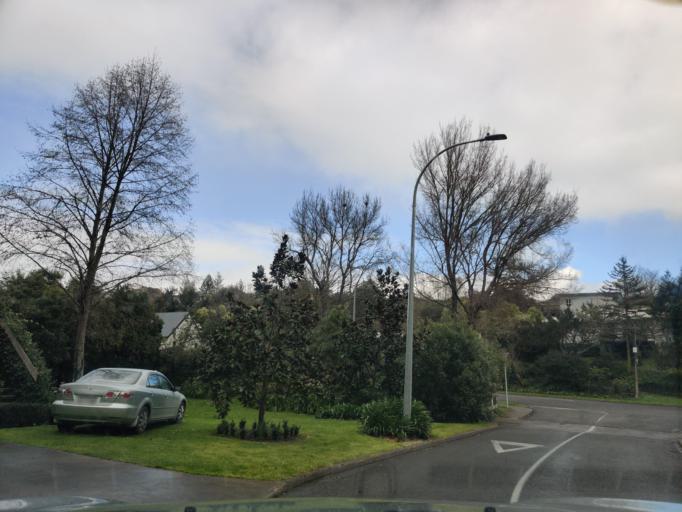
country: NZ
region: Hawke's Bay
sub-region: Hastings District
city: Hastings
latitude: -39.6760
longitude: 176.8944
